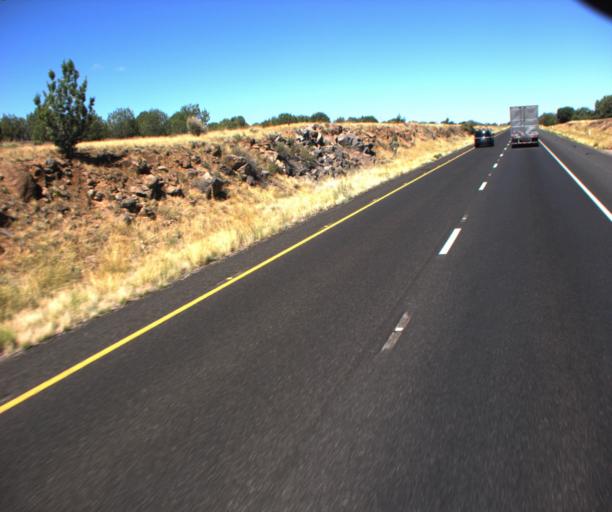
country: US
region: Arizona
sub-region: Yavapai County
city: Paulden
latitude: 35.2549
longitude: -112.7031
